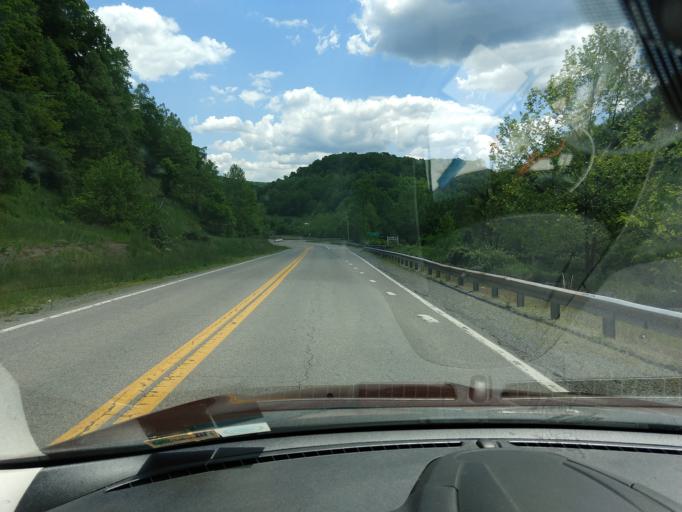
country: US
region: West Virginia
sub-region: Gilmer County
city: Glenville
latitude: 38.9293
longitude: -80.7888
